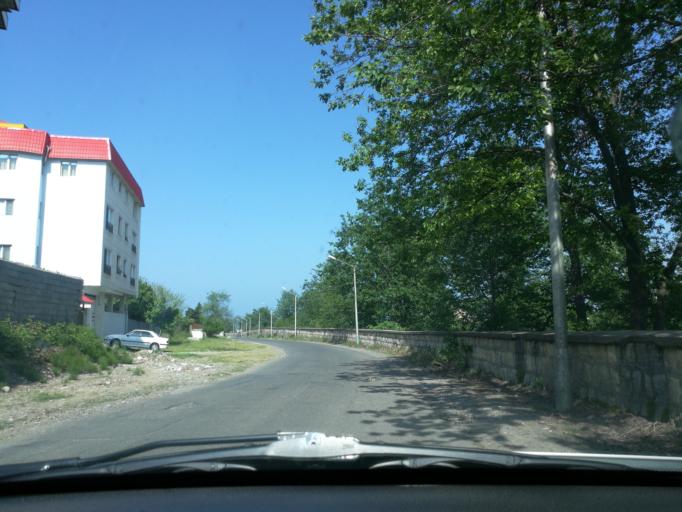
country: IR
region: Mazandaran
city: Chalus
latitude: 36.6566
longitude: 51.4294
